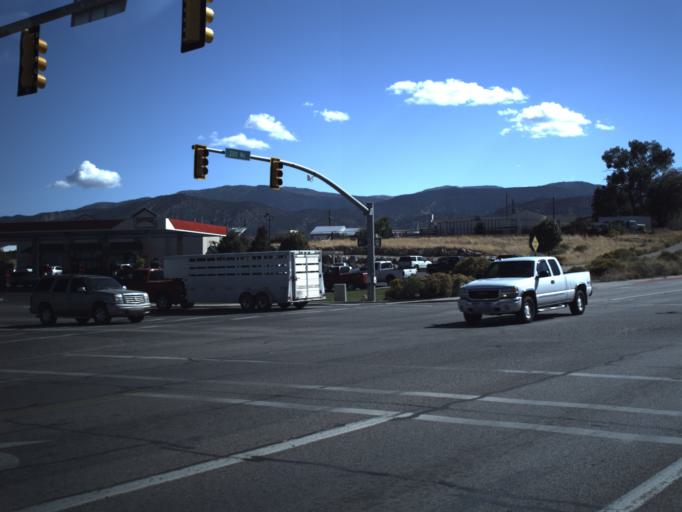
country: US
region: Utah
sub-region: Iron County
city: Cedar City
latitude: 37.6813
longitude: -113.0865
